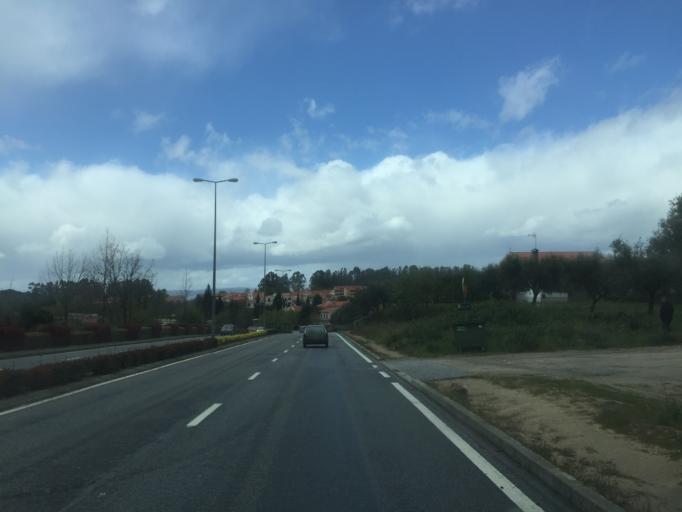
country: PT
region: Guarda
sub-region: Manteigas
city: Manteigas
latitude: 40.4993
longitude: -7.6042
